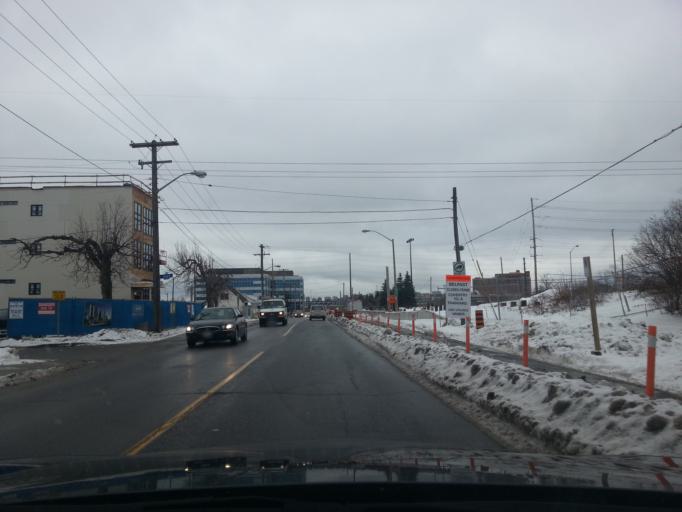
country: CA
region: Ontario
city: Ottawa
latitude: 45.4187
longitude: -75.6457
